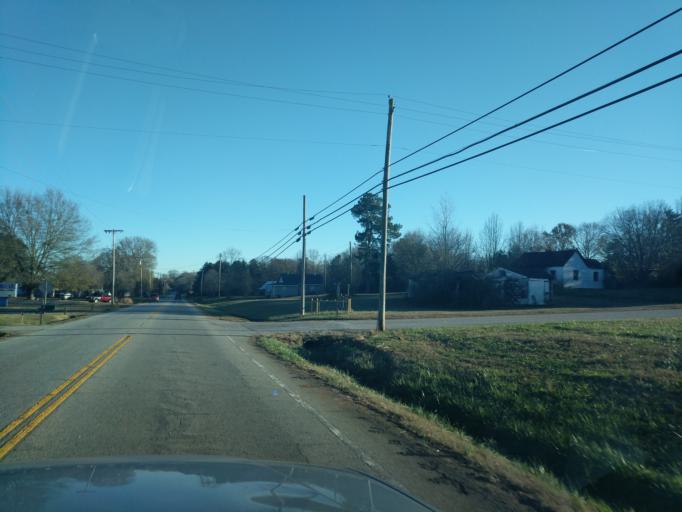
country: US
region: South Carolina
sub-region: Oconee County
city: Westminster
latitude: 34.6785
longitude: -83.1157
